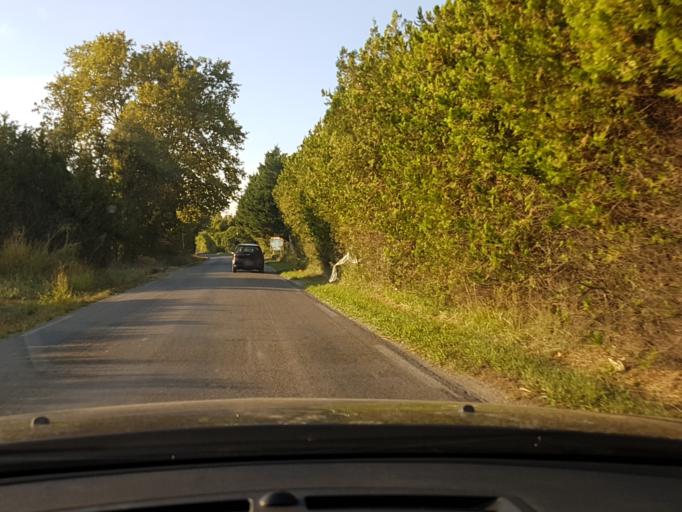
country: FR
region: Provence-Alpes-Cote d'Azur
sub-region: Departement des Bouches-du-Rhone
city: Molleges
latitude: 43.8158
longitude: 4.9480
